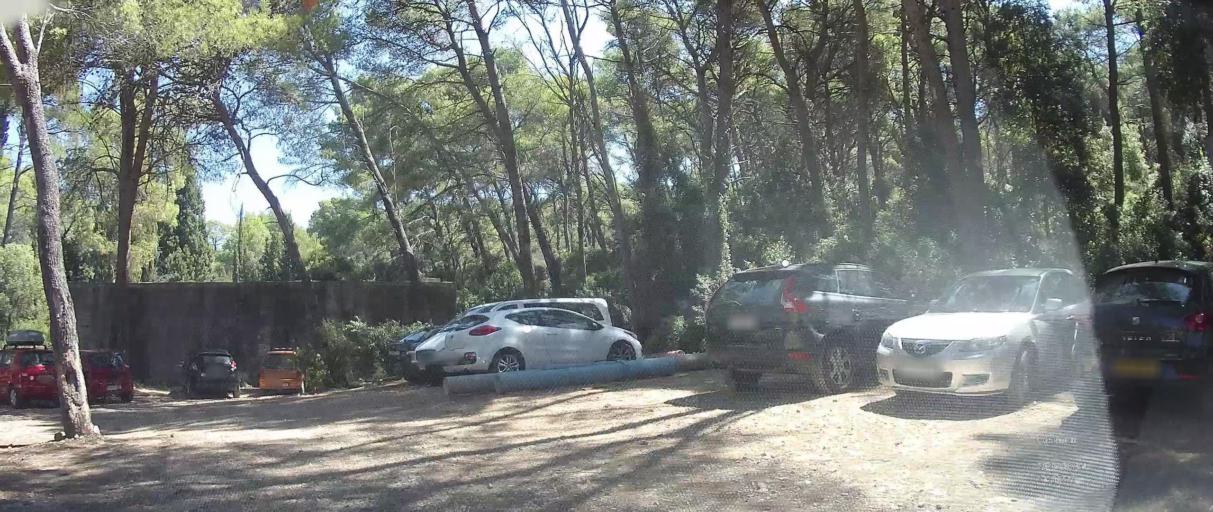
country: HR
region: Dubrovacko-Neretvanska
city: Blato
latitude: 42.7784
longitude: 17.3687
